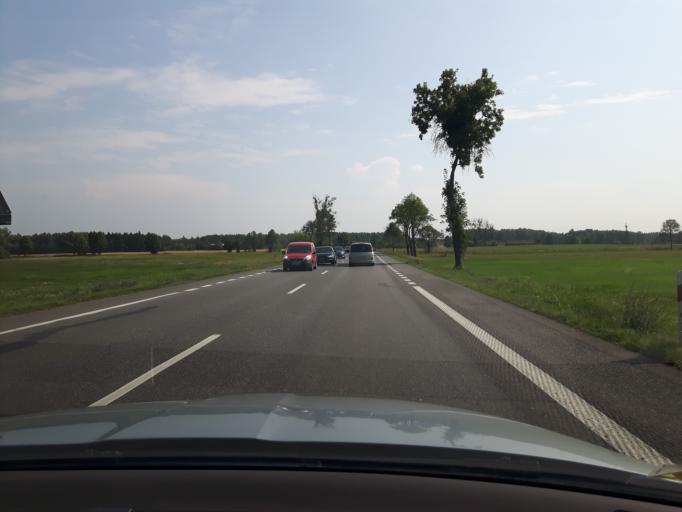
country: PL
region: Masovian Voivodeship
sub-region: Powiat mlawski
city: Strzegowo
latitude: 52.9344
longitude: 20.2843
